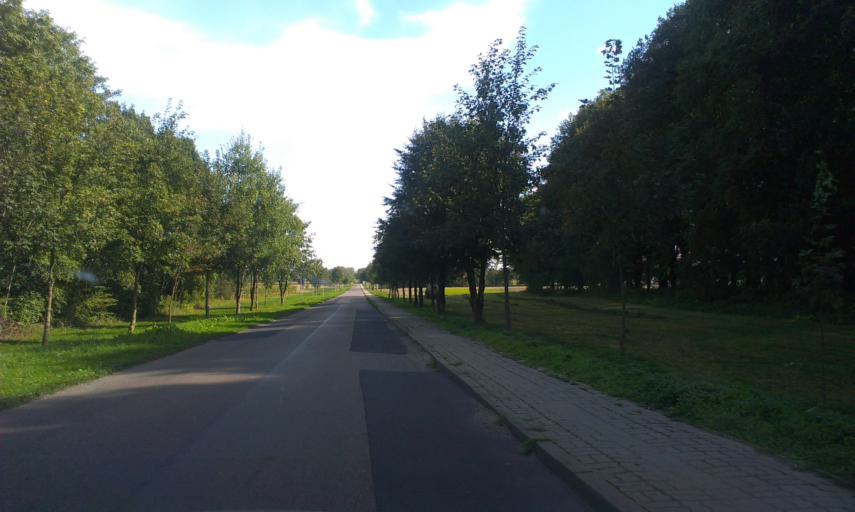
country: PL
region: Greater Poland Voivodeship
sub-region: Powiat pilski
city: Lobzenica
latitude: 53.2706
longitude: 17.2399
